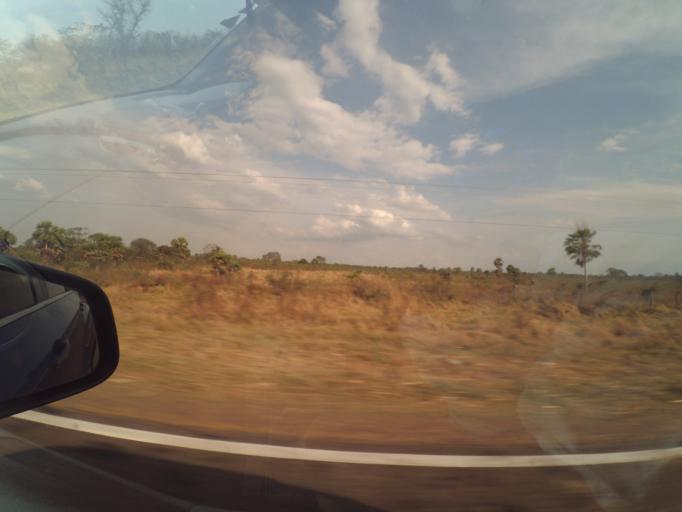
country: BO
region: Santa Cruz
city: Montero
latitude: -17.2680
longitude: -63.0817
